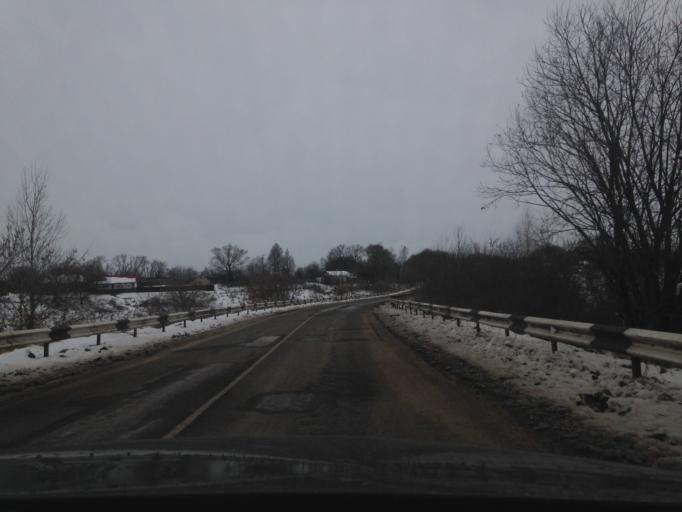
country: RU
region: Tula
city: Teploye
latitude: 53.7743
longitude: 37.6410
